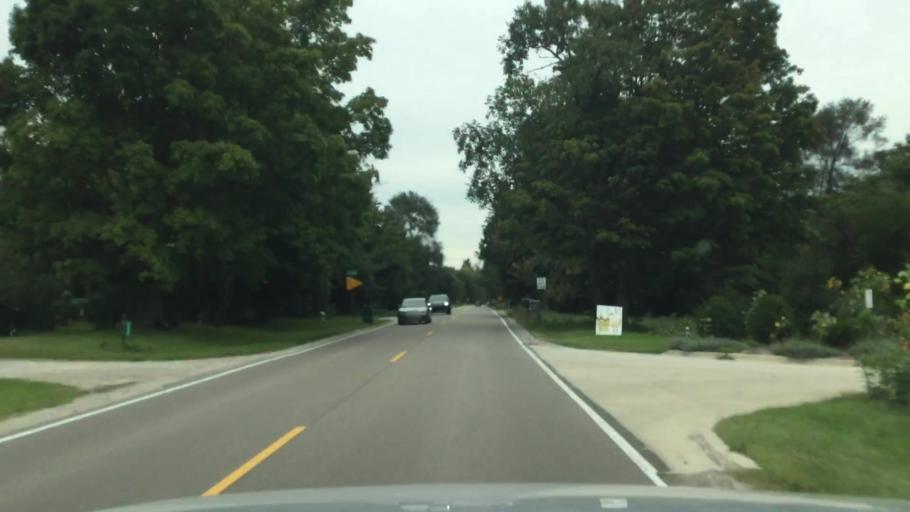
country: US
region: Michigan
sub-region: Washtenaw County
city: Ypsilanti
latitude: 42.1917
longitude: -83.6332
